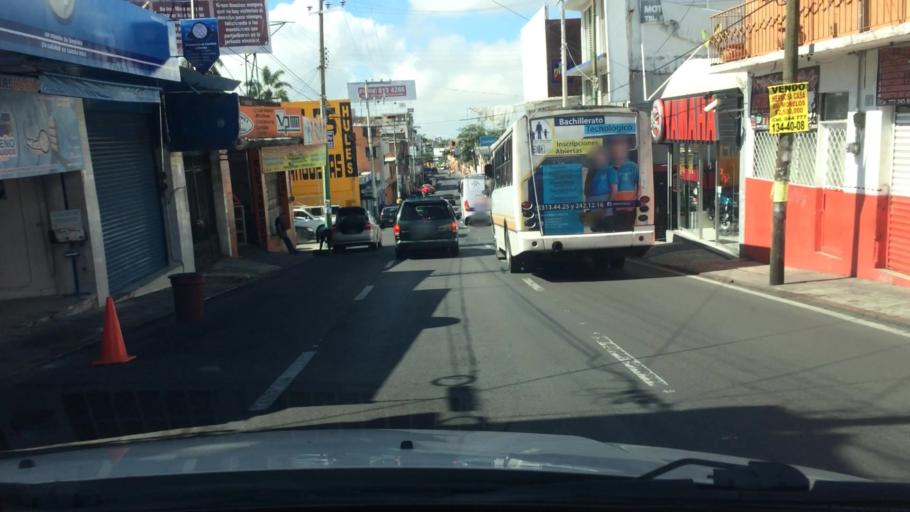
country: MX
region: Morelos
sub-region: Cuernavaca
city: Cuernavaca
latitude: 18.9356
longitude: -99.2406
